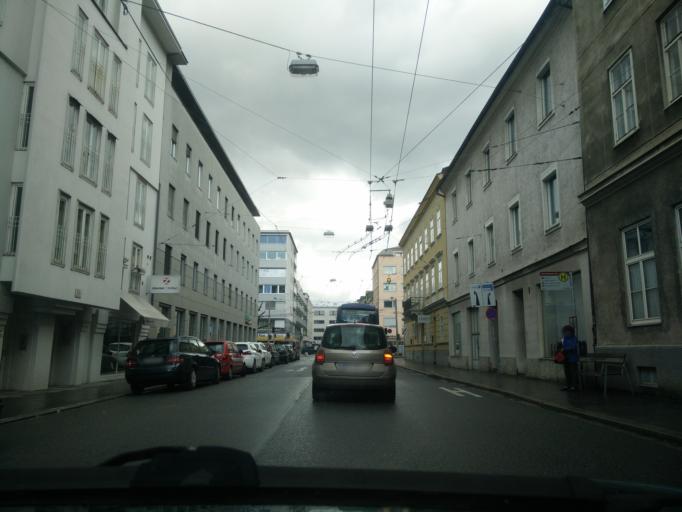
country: AT
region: Salzburg
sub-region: Salzburg Stadt
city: Salzburg
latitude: 47.8057
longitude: 13.0477
